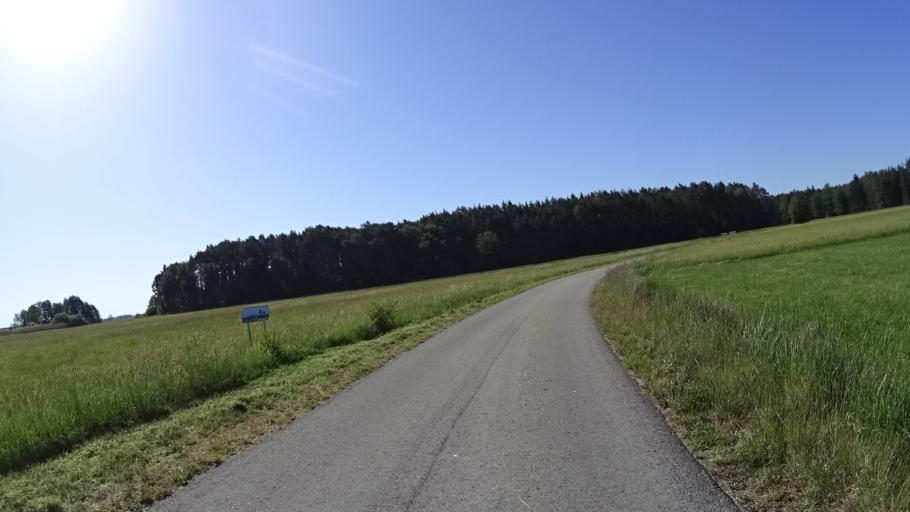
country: DE
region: Bavaria
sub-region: Regierungsbezirk Mittelfranken
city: Arberg
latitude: 49.1591
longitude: 10.5948
